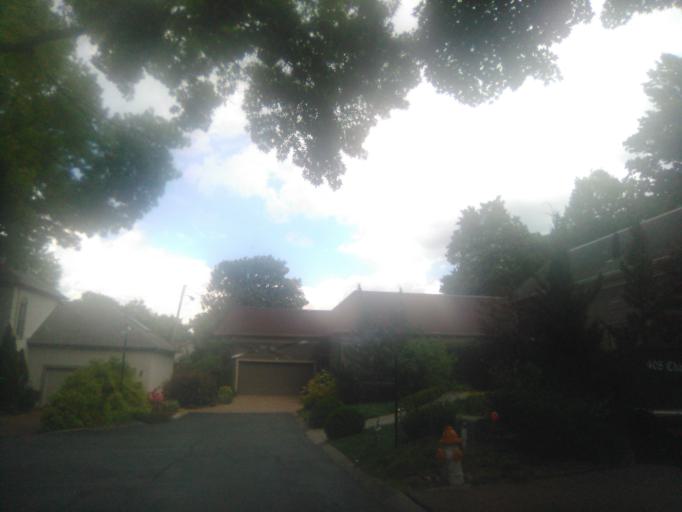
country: US
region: Tennessee
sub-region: Davidson County
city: Belle Meade
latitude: 36.1095
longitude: -86.8318
